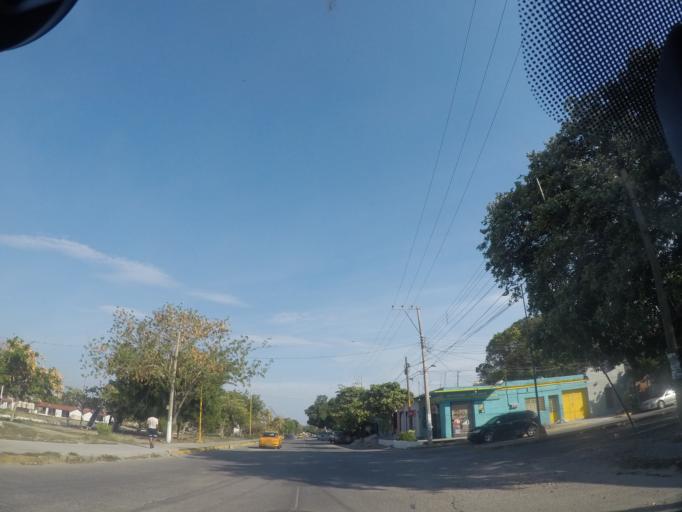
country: MX
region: Oaxaca
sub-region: Salina Cruz
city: Salina Cruz
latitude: 16.1821
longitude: -95.1996
